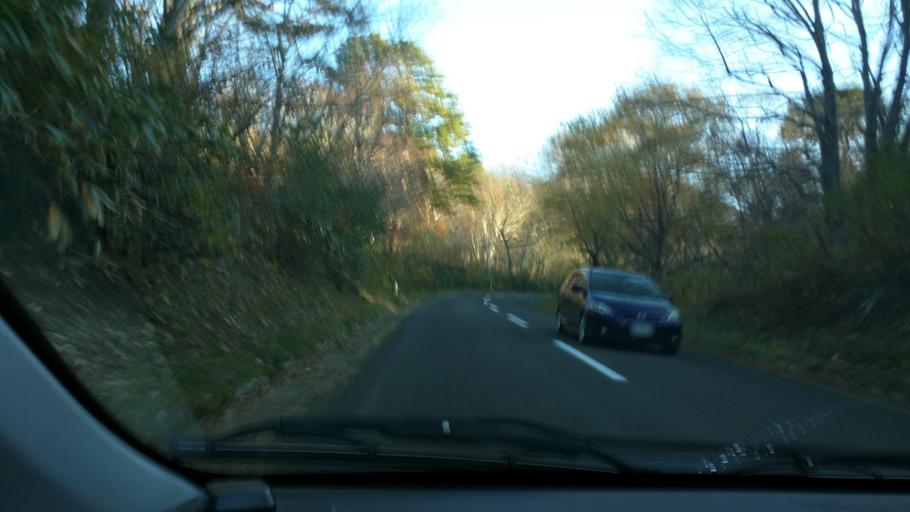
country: JP
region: Fukushima
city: Inawashiro
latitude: 37.6273
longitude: 140.0516
